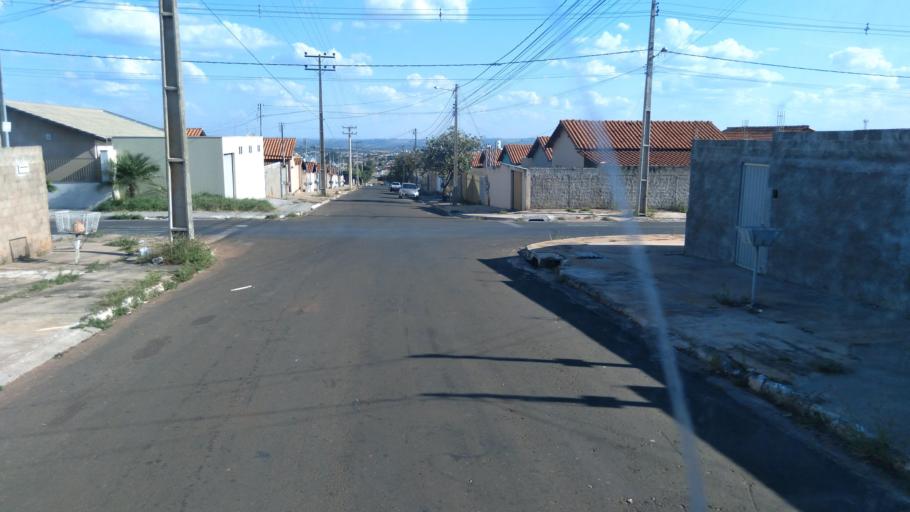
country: BR
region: Goias
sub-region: Mineiros
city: Mineiros
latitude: -17.5463
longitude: -52.5395
